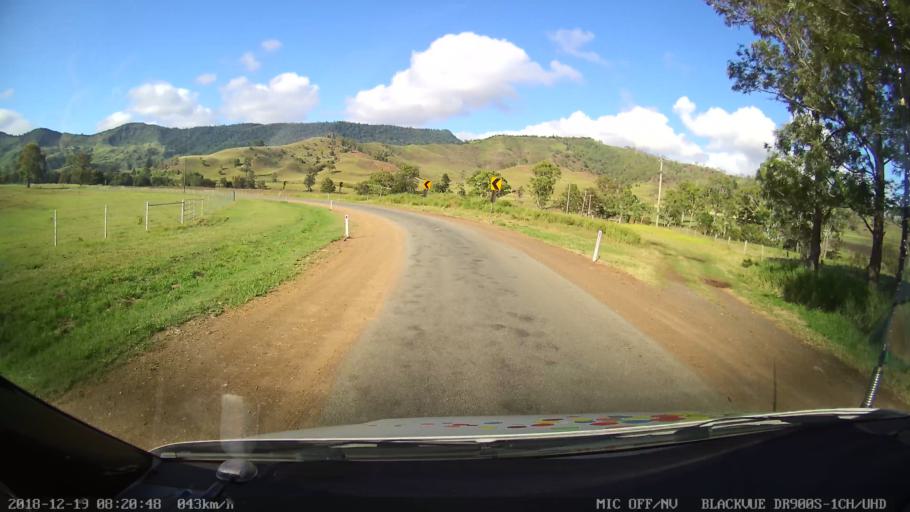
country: AU
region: New South Wales
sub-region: Kyogle
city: Kyogle
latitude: -28.2925
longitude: 152.9094
